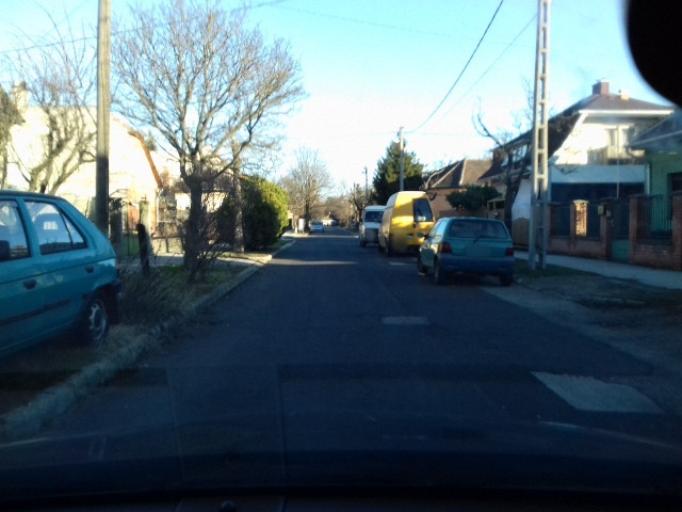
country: HU
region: Budapest
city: Budapest IV. keruelet
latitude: 47.5840
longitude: 19.0875
